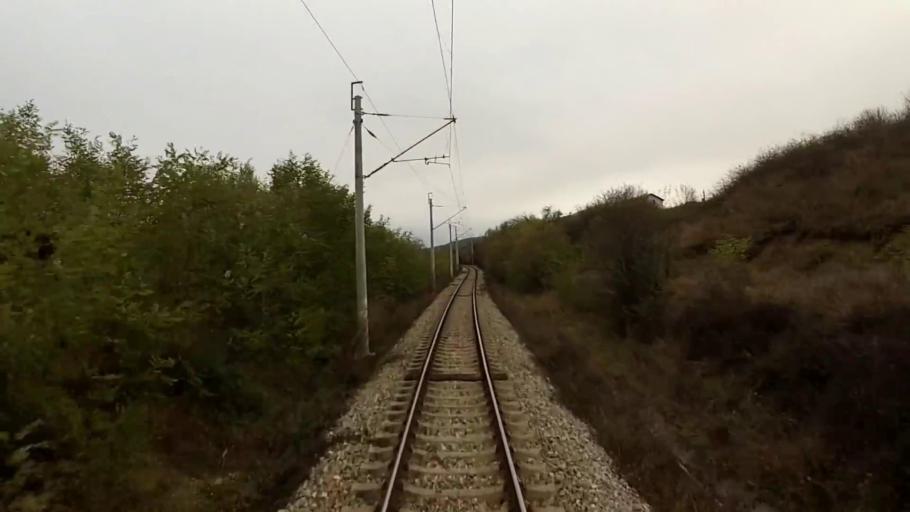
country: BG
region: Sofiya
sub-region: Obshtina Dragoman
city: Dragoman
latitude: 42.9370
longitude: 22.9034
